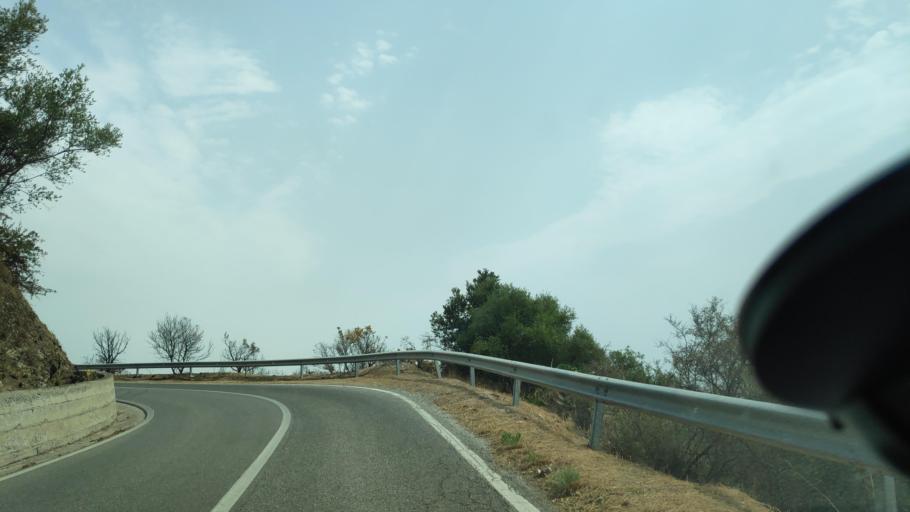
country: IT
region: Calabria
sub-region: Provincia di Catanzaro
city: Sant'Andrea Apostolo dello Ionio
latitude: 38.6448
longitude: 16.5311
